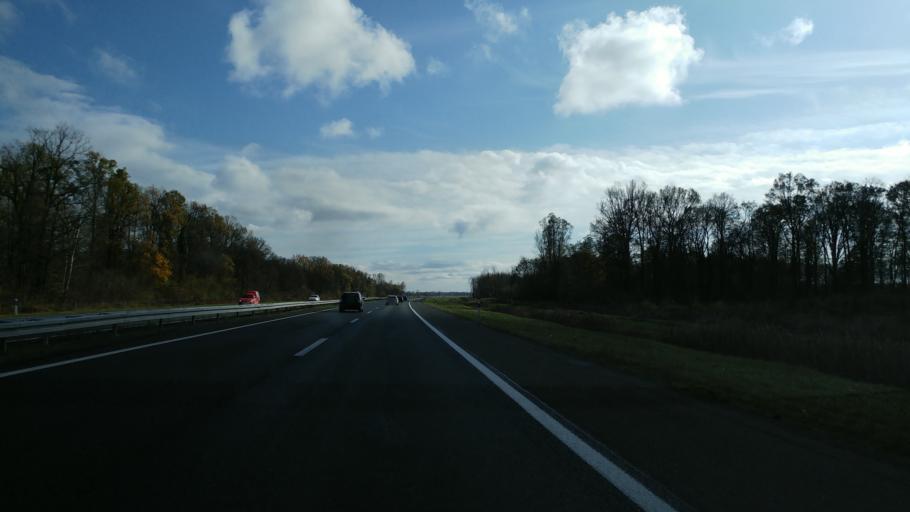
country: HR
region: Zagrebacka
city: Lupoglav
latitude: 45.7399
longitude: 16.3284
